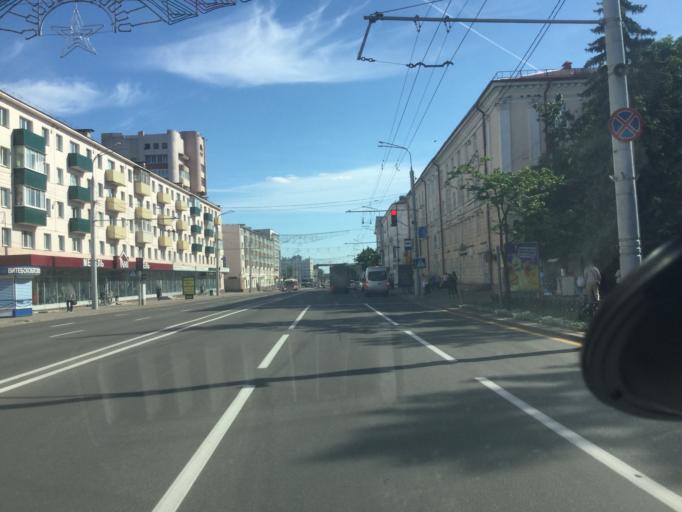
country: BY
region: Vitebsk
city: Vitebsk
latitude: 55.1869
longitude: 30.2049
